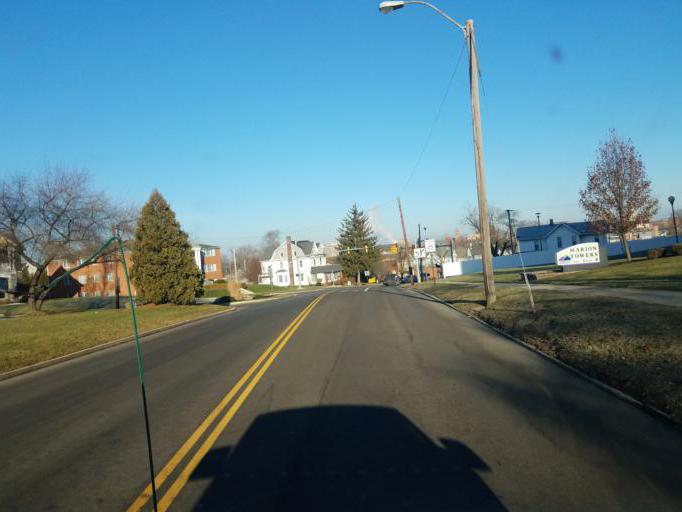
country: US
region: Ohio
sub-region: Marion County
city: Marion
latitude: 40.5818
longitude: -83.1279
